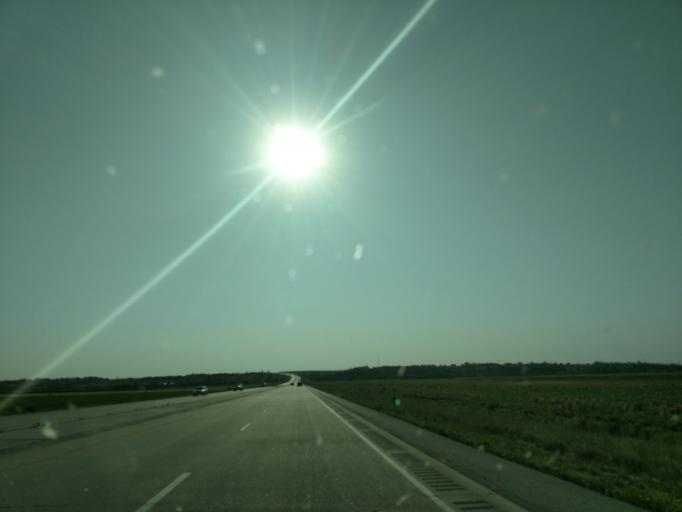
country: US
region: Nebraska
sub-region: Sarpy County
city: Offutt Air Force Base
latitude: 41.0789
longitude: -95.8992
